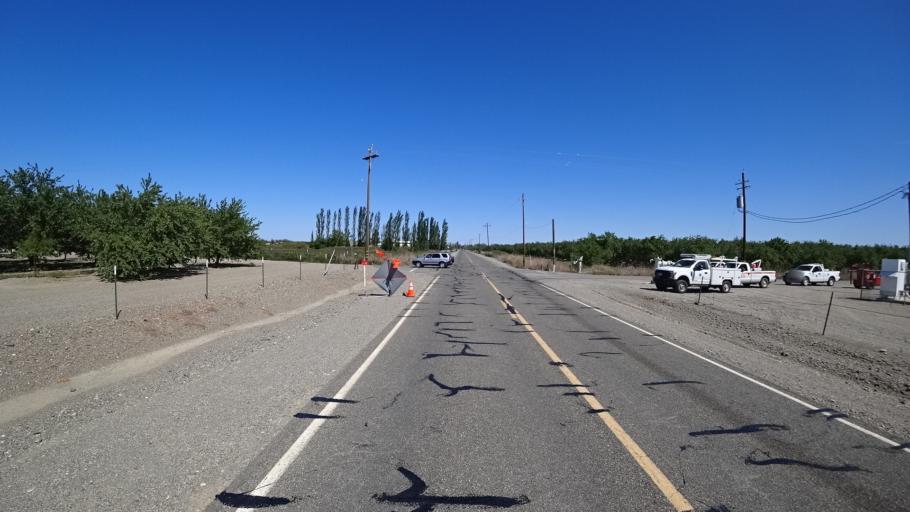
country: US
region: California
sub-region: Glenn County
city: Orland
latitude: 39.7321
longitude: -122.1410
